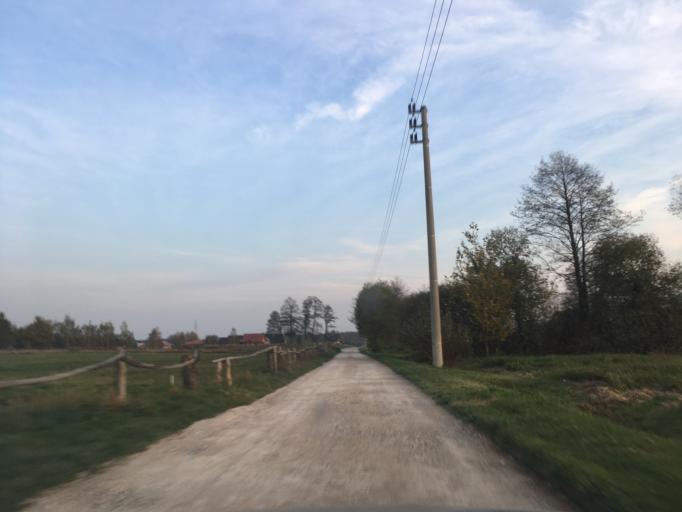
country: PL
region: Masovian Voivodeship
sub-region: Powiat piaseczynski
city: Lesznowola
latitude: 52.0506
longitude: 20.9256
